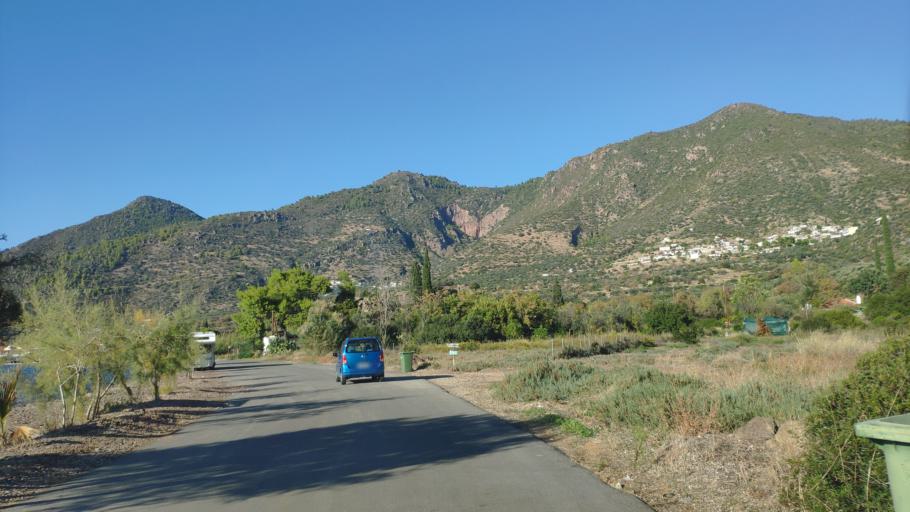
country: GR
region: Attica
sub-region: Nomos Piraios
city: Megalochori
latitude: 37.5836
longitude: 23.3491
